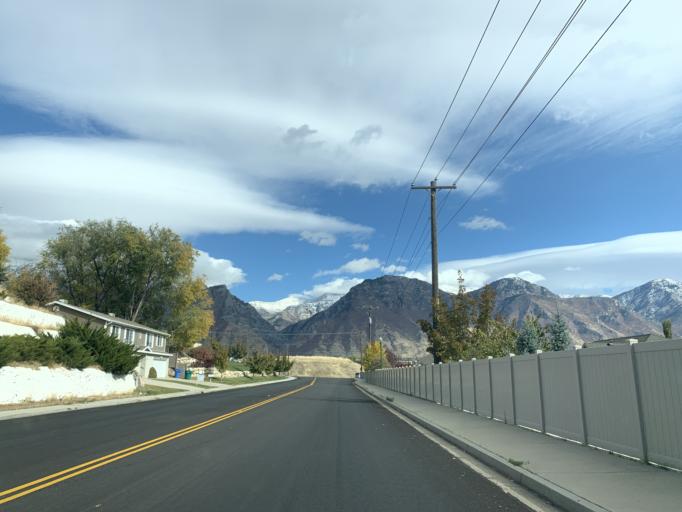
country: US
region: Utah
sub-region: Utah County
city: Provo
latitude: 40.2606
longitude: -111.6825
